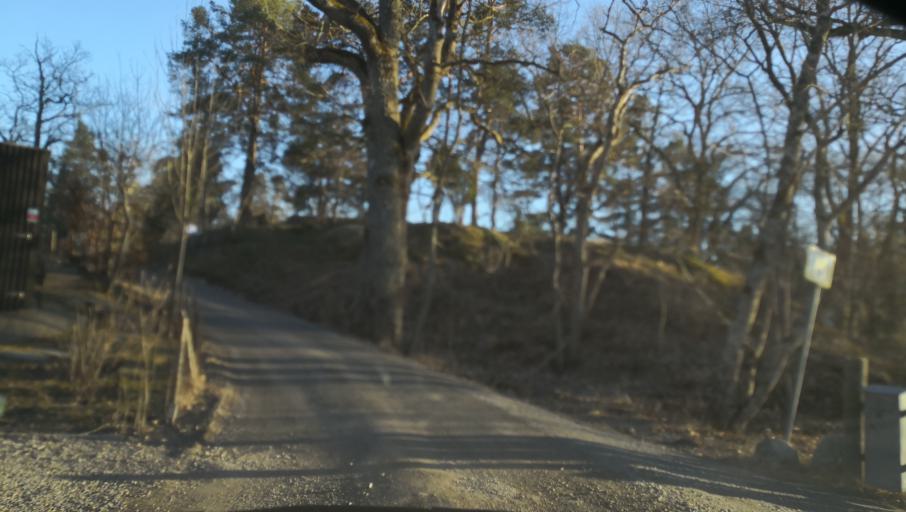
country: SE
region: Stockholm
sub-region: Varmdo Kommun
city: Mortnas
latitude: 59.3321
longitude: 18.4332
